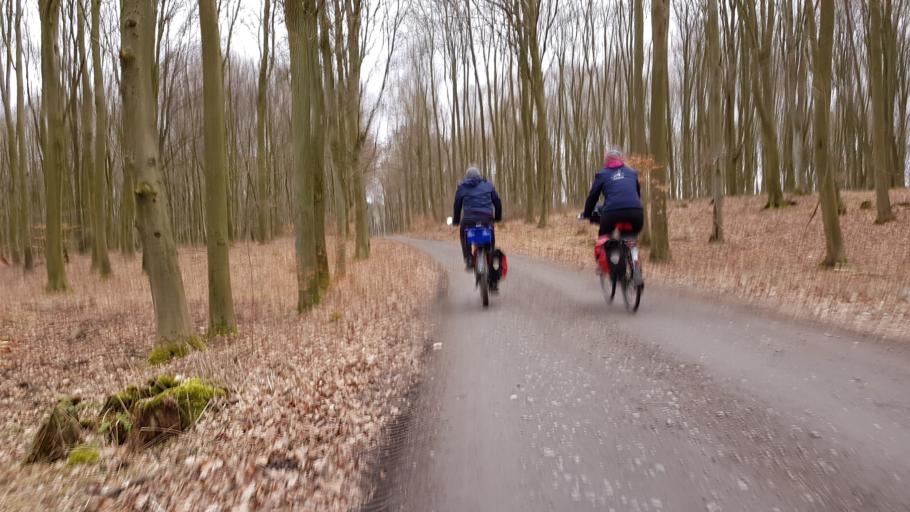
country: PL
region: West Pomeranian Voivodeship
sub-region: Powiat gryfinski
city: Banie
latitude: 53.0710
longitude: 14.7352
